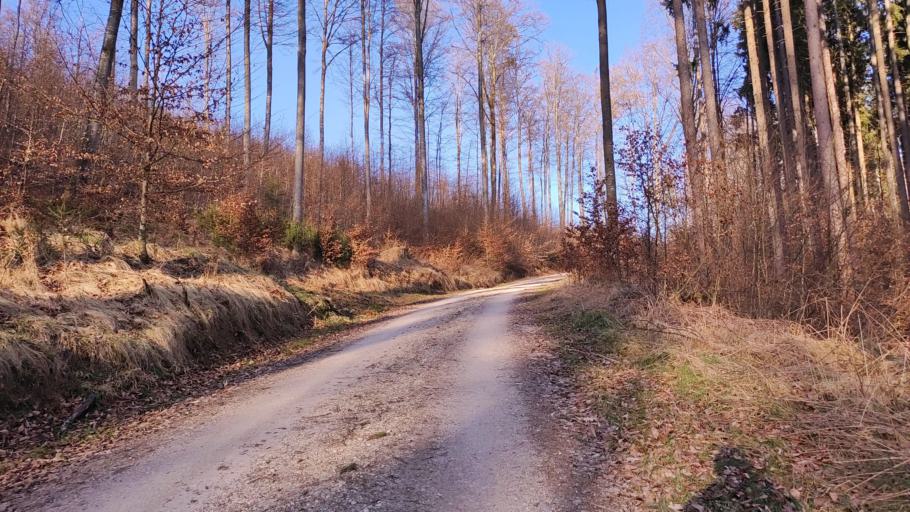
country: DE
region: Bavaria
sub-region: Swabia
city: Zusmarshausen
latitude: 48.4269
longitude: 10.6169
